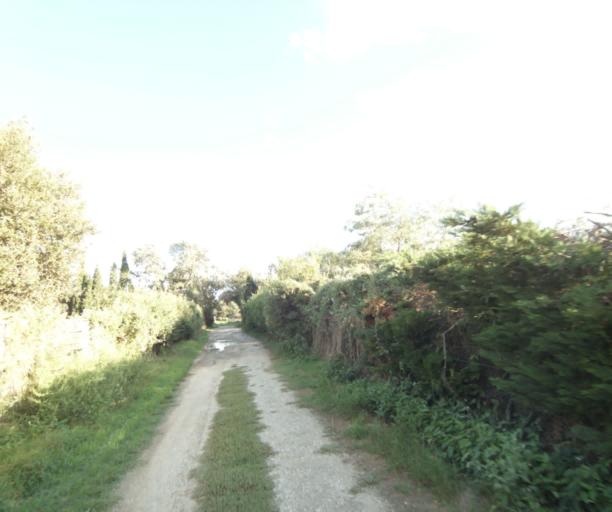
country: FR
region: Languedoc-Roussillon
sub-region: Departement des Pyrenees-Orientales
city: Argelers
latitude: 42.5657
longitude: 3.0202
